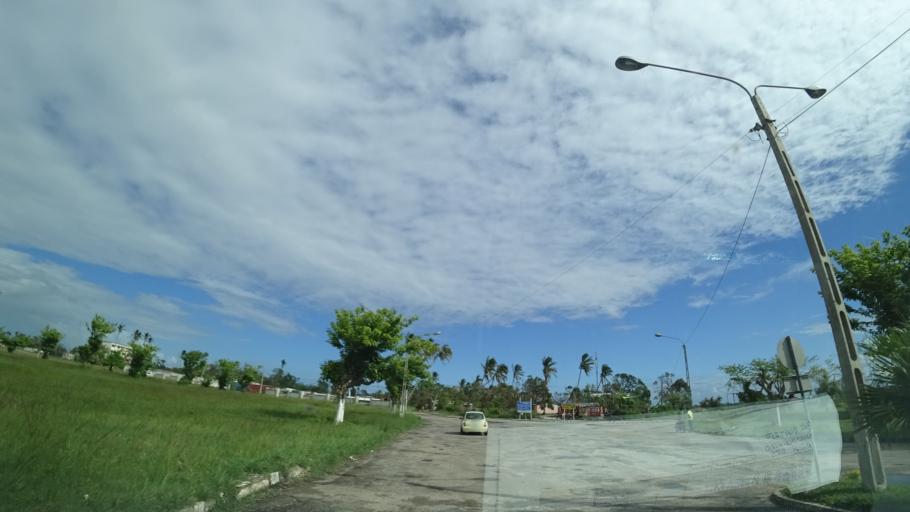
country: MZ
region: Sofala
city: Beira
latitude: -19.8005
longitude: 34.9001
